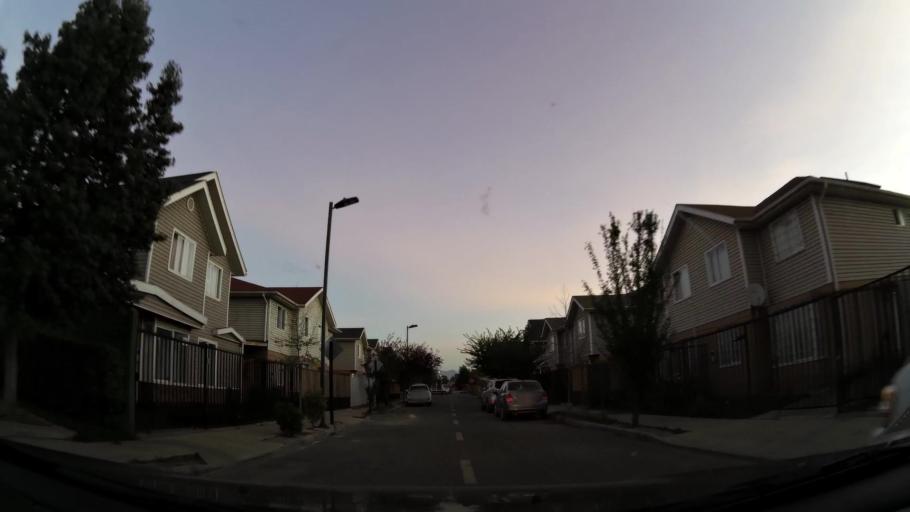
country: CL
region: Santiago Metropolitan
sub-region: Provincia de Cordillera
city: Puente Alto
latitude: -33.5974
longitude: -70.5916
